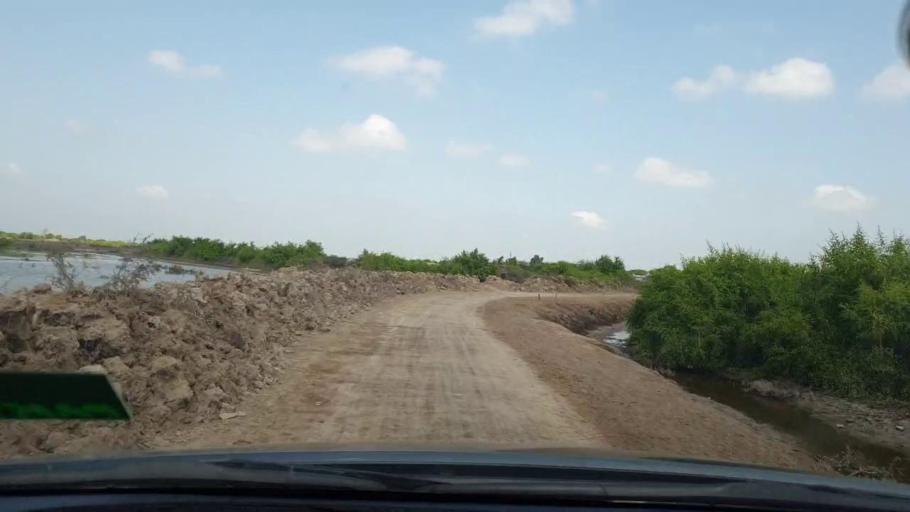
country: PK
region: Sindh
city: Tando Bago
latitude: 24.9546
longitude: 69.0756
